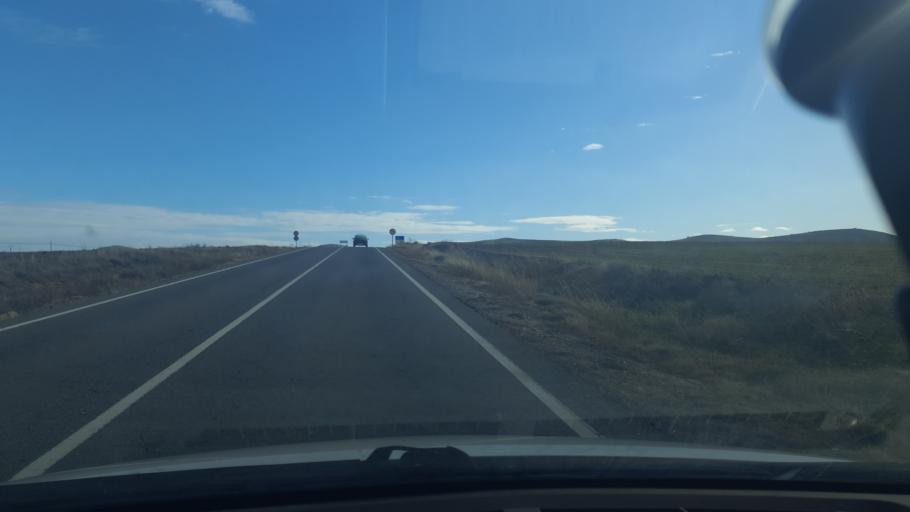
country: ES
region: Castille and Leon
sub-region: Provincia de Avila
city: Penalba de Avila
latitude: 40.7859
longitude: -4.7580
